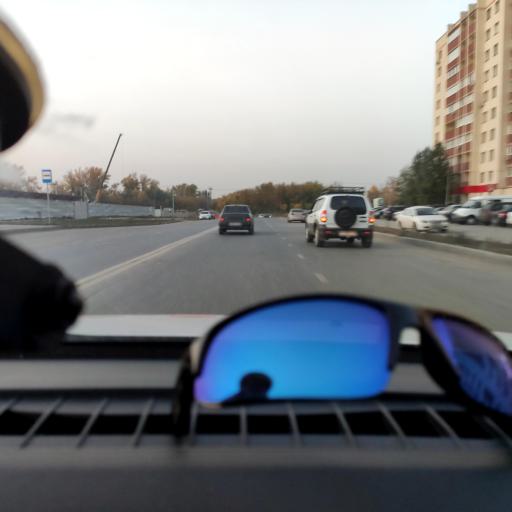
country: RU
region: Samara
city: Rozhdestveno
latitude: 53.1565
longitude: 50.0756
